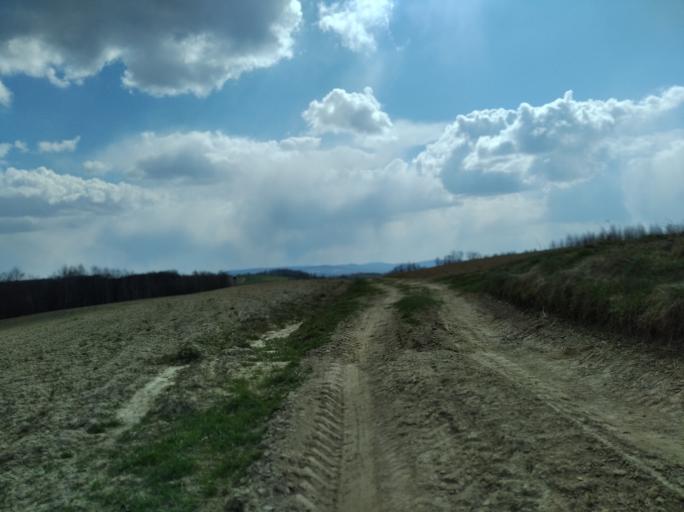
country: PL
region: Subcarpathian Voivodeship
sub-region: Powiat strzyzowski
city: Strzyzow
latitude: 49.9190
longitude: 21.7439
